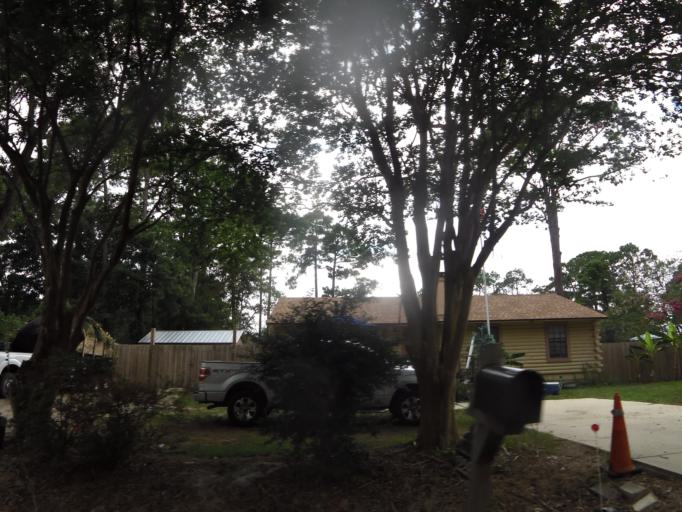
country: US
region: Florida
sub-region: Duval County
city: Atlantic Beach
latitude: 30.3342
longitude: -81.4201
